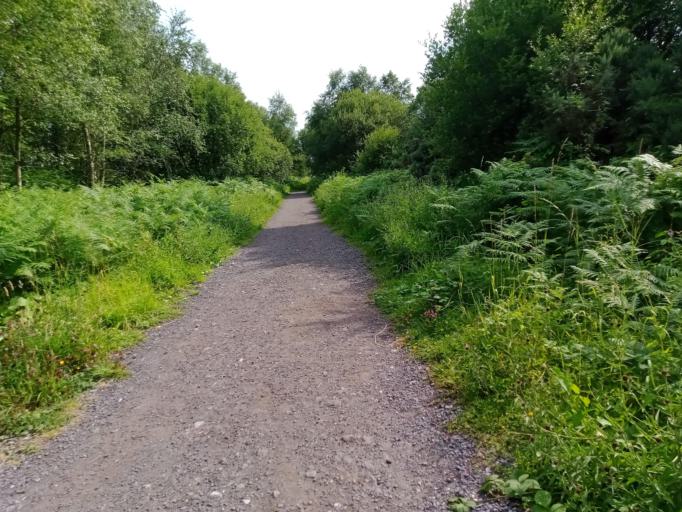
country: IE
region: Leinster
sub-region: Laois
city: Abbeyleix
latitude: 52.8938
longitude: -7.3503
